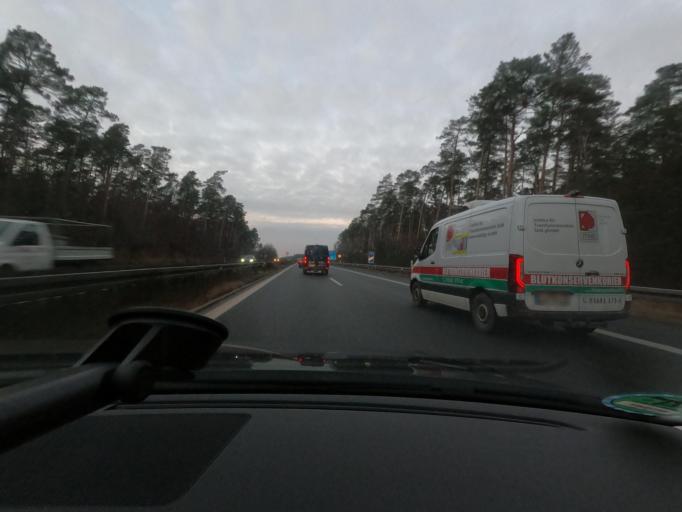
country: DE
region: Bavaria
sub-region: Upper Franconia
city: Memmelsdorf
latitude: 49.8989
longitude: 10.9479
